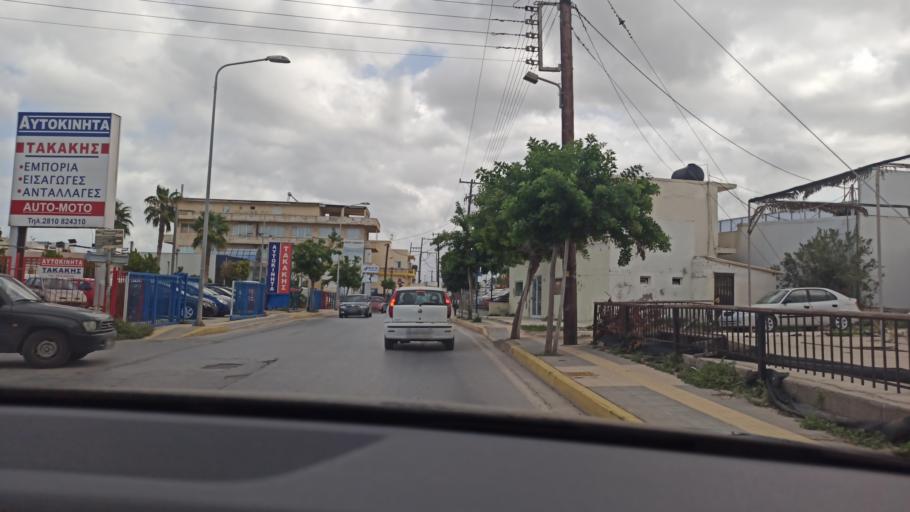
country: GR
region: Crete
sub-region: Nomos Irakleiou
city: Gazi
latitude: 35.3337
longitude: 25.0960
